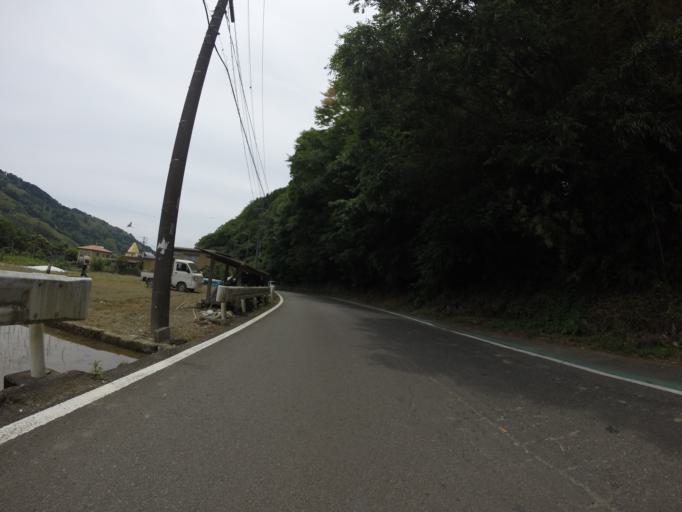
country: JP
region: Shizuoka
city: Shizuoka-shi
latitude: 35.0391
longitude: 138.4258
